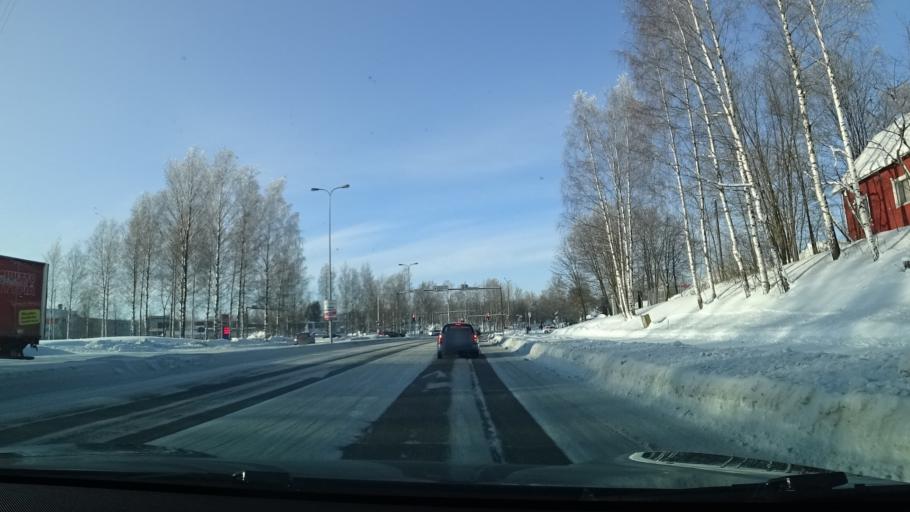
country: FI
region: South Karelia
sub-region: Lappeenranta
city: Lappeenranta
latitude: 61.0463
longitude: 28.2034
